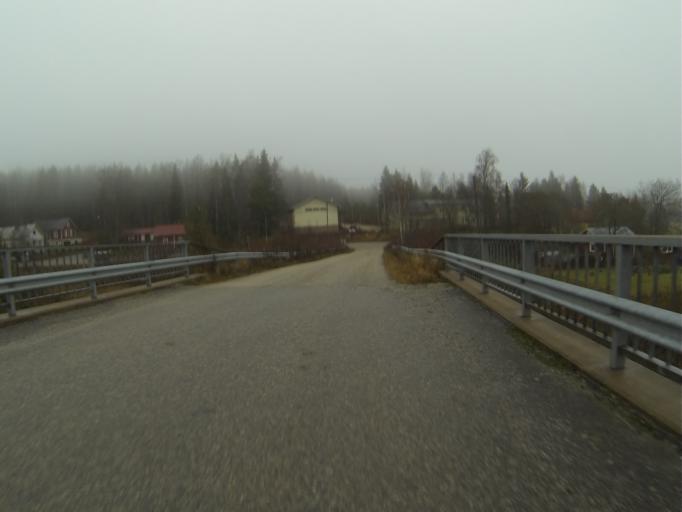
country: FI
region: Varsinais-Suomi
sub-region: Salo
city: Halikko
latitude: 60.4156
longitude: 22.9265
